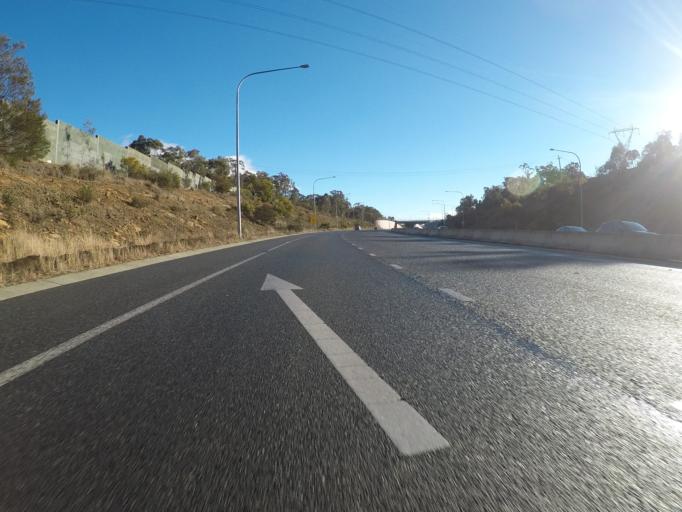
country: AU
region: Australian Capital Territory
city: Macquarie
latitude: -35.2651
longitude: 149.0858
